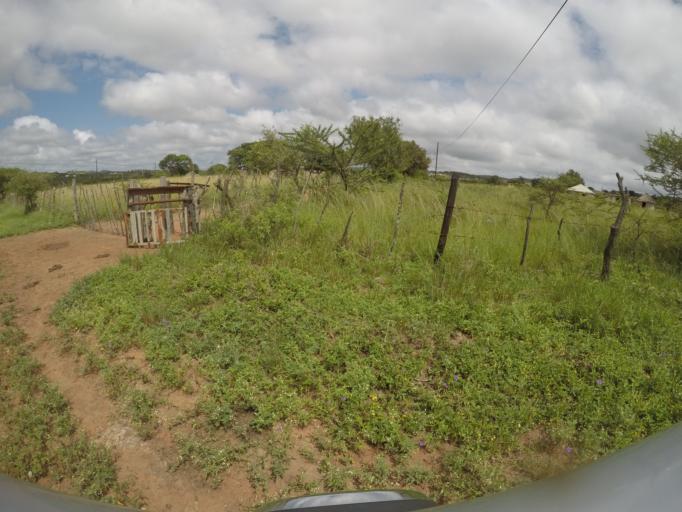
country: ZA
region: KwaZulu-Natal
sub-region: uThungulu District Municipality
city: Empangeni
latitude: -28.5861
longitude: 31.8481
